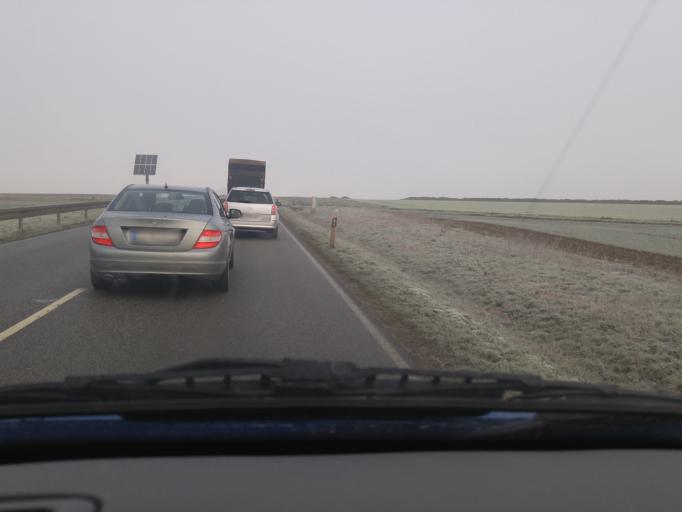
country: DE
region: Hesse
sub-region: Regierungsbezirk Darmstadt
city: Friedberg
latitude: 50.3048
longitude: 8.7493
